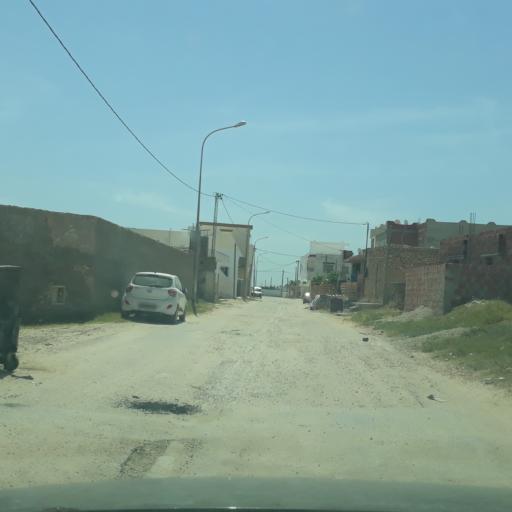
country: TN
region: Safaqis
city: Al Qarmadah
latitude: 34.8246
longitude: 10.7800
